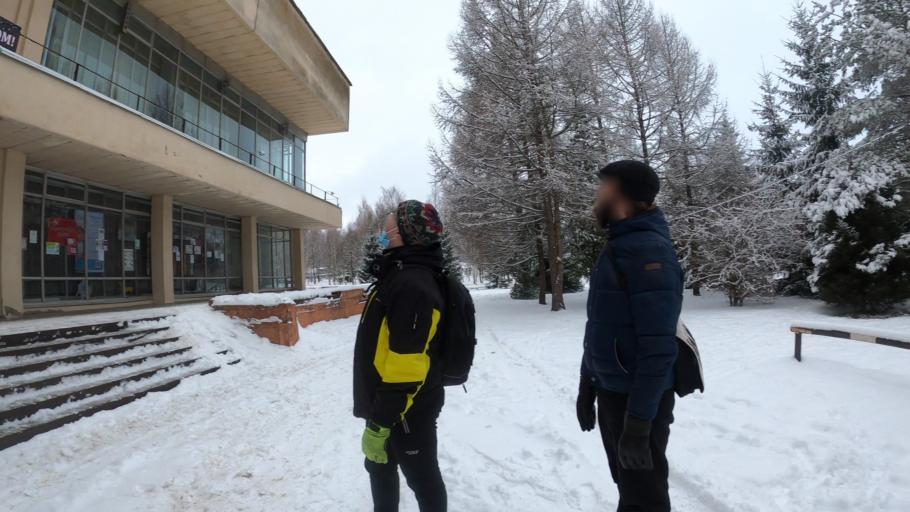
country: RU
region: Jaroslavl
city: Pereslavl'-Zalesskiy
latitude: 56.7523
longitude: 38.8881
